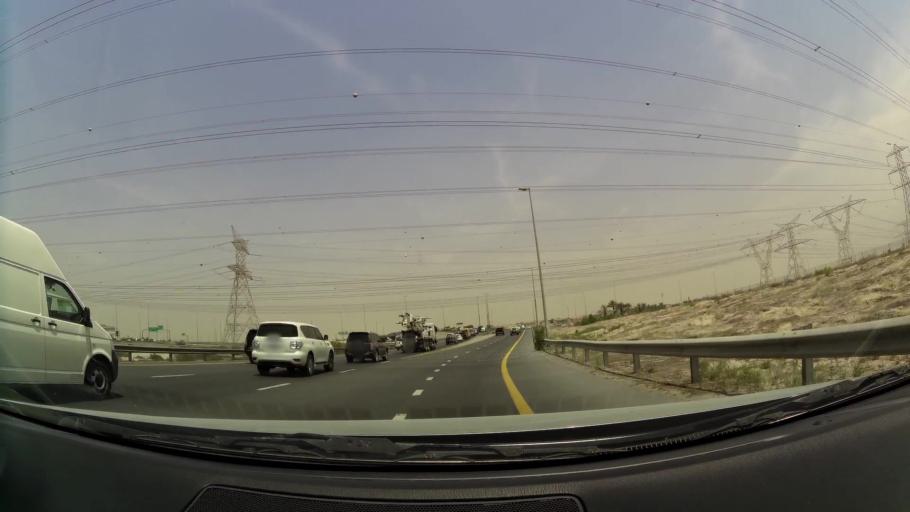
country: AE
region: Ash Shariqah
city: Sharjah
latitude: 25.2118
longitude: 55.3986
